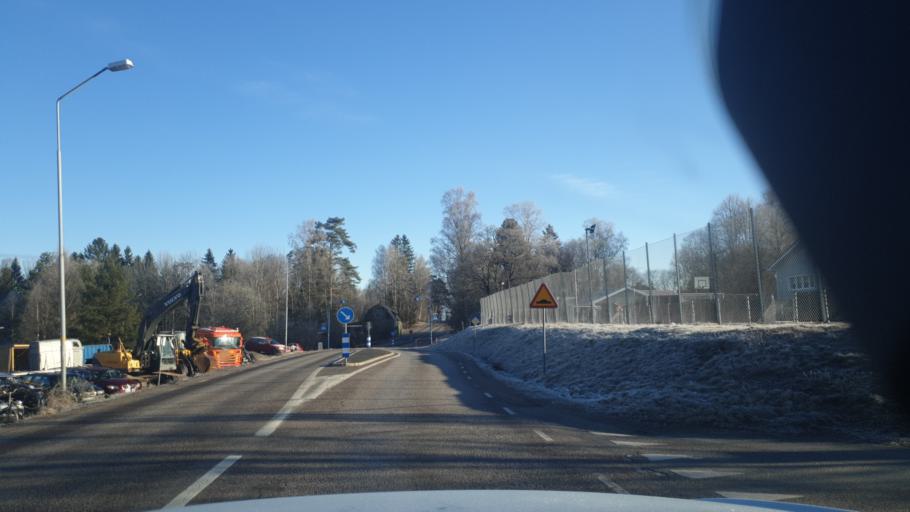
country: SE
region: Vaermland
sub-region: Eda Kommun
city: Amotfors
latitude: 59.7006
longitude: 12.1471
